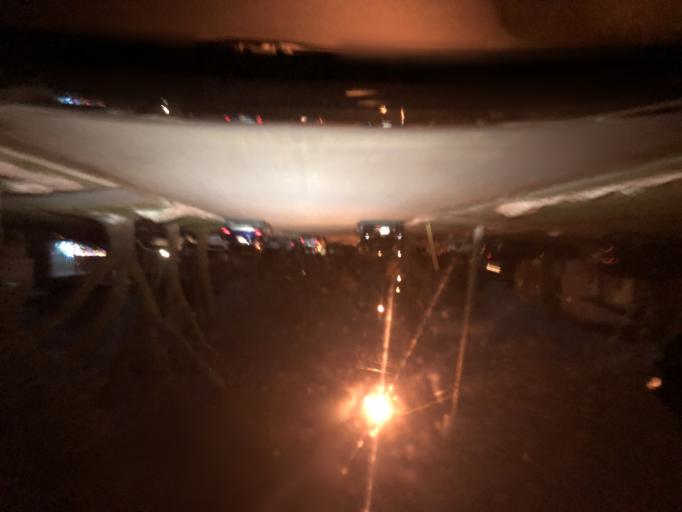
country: CA
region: Ontario
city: Scarborough
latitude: 43.7789
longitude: -79.3008
